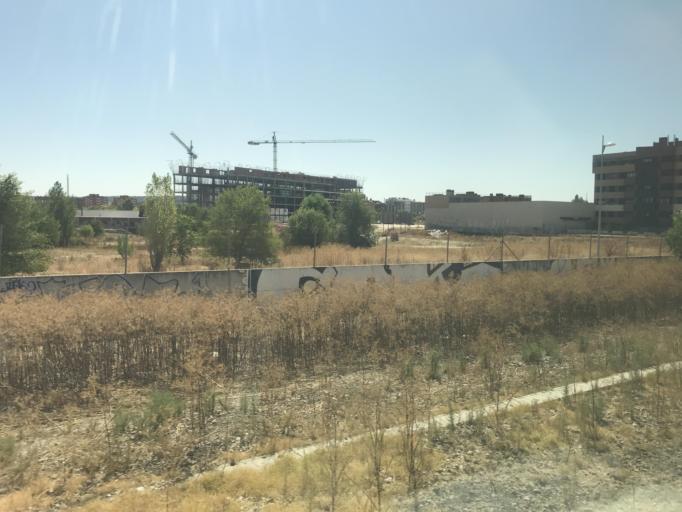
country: ES
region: Castille and Leon
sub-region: Provincia de Valladolid
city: Valladolid
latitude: 41.6573
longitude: -4.7061
